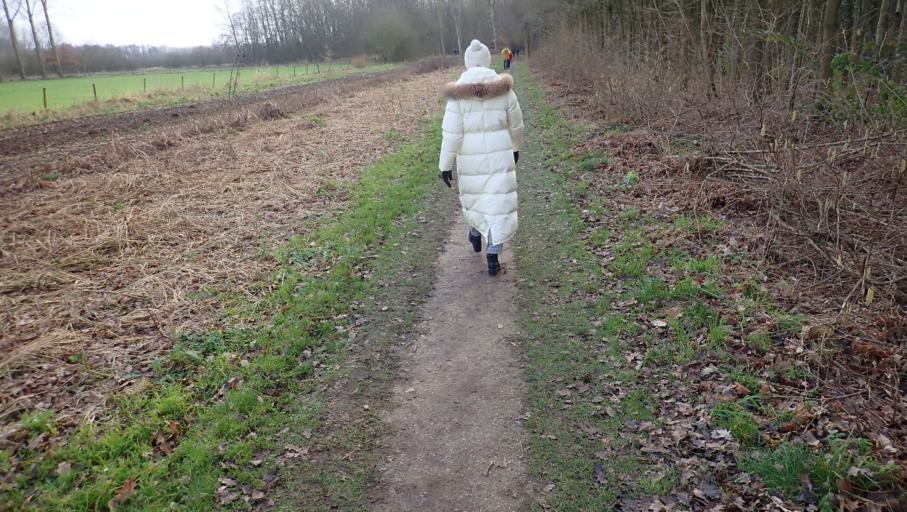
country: BE
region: Flanders
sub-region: Provincie Antwerpen
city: Berlaar
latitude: 51.1356
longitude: 4.6303
